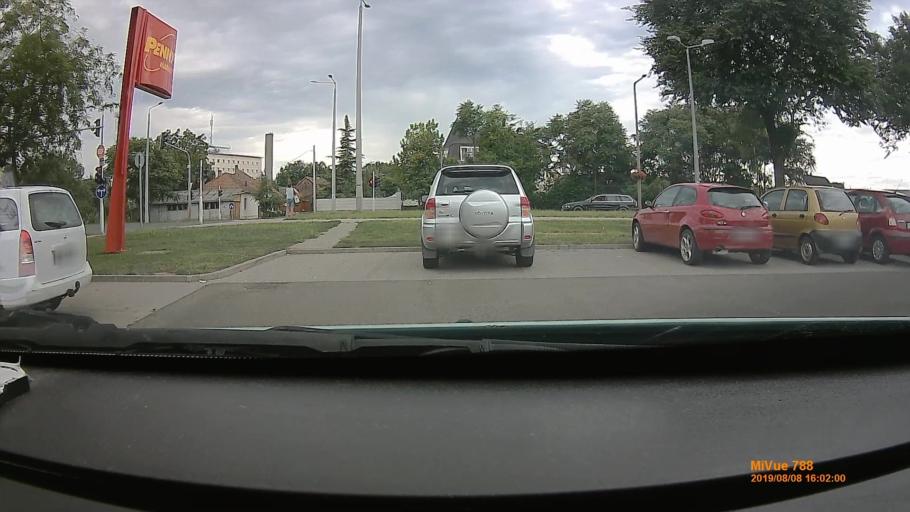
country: HU
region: Szabolcs-Szatmar-Bereg
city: Mateszalka
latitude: 47.9569
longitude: 22.3251
